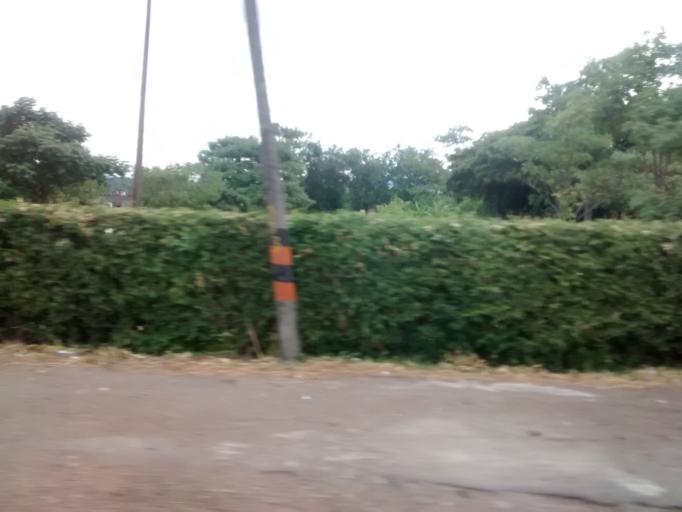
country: CO
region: Tolima
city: Melgar
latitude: 4.2232
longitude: -74.6956
